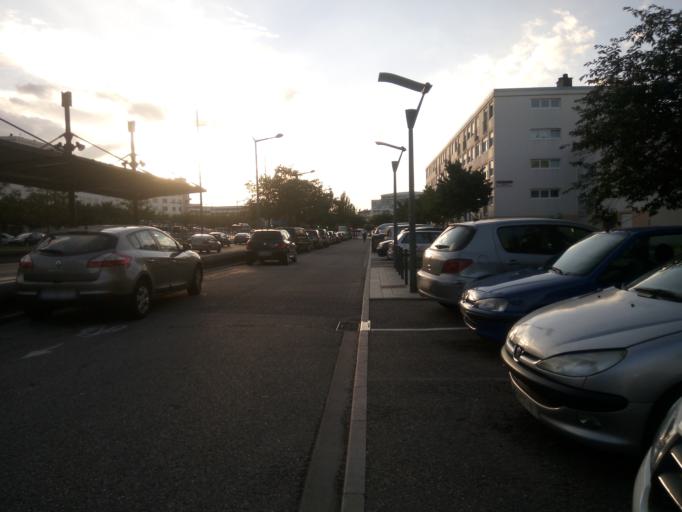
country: FR
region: Lorraine
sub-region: Departement de Meurthe-et-Moselle
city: Villers-les-Nancy
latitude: 48.6647
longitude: 6.1691
